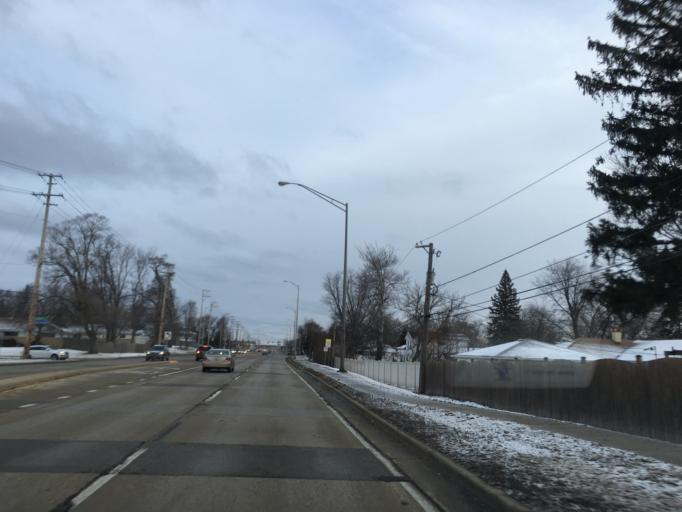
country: US
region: Illinois
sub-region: Cook County
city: Hoffman Estates
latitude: 42.0393
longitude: -88.0797
